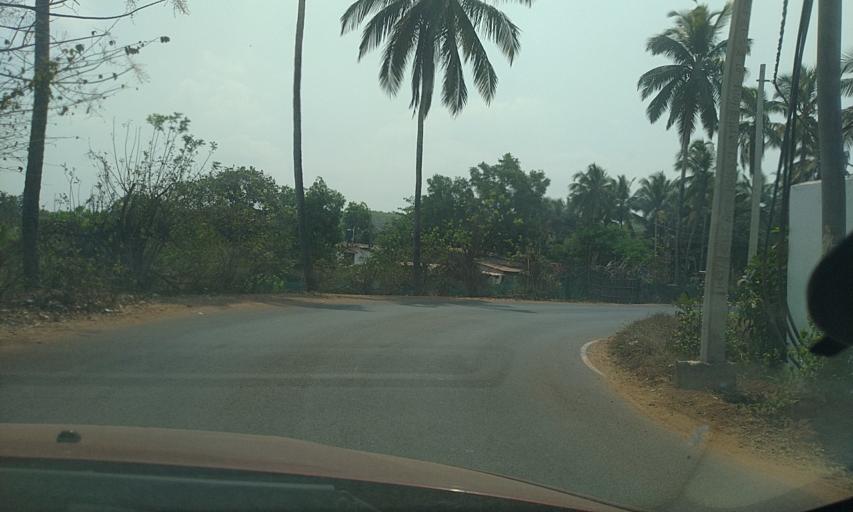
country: IN
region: Goa
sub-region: North Goa
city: Vagator
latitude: 15.5906
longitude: 73.7645
